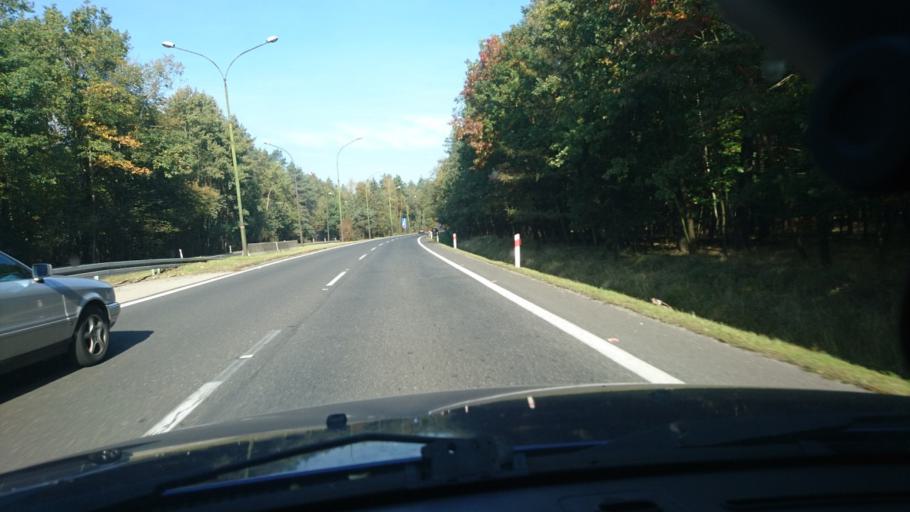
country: PL
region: Silesian Voivodeship
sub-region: Katowice
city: Murcki
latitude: 50.1616
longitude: 19.0187
